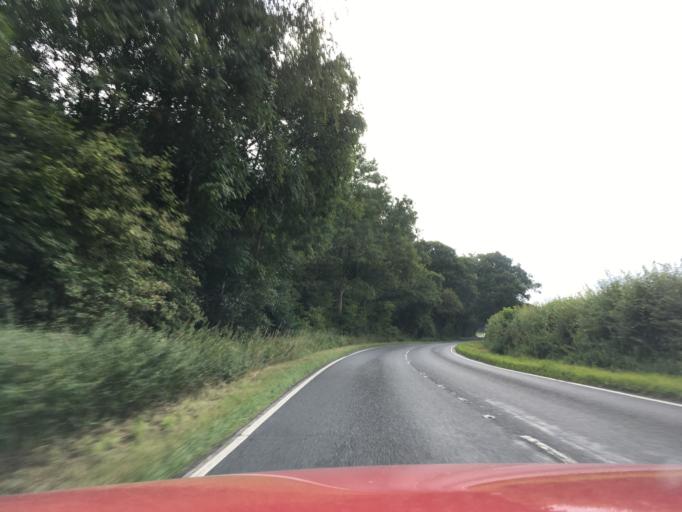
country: GB
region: England
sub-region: Hampshire
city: Four Marks
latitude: 51.0306
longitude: -1.0598
